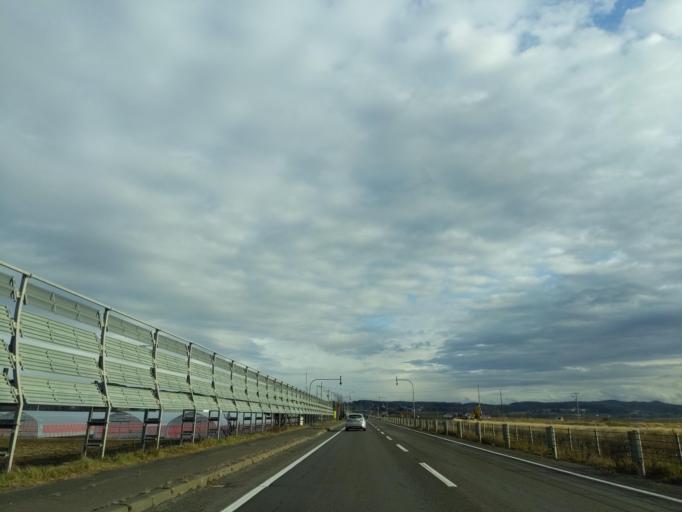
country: JP
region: Hokkaido
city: Kitahiroshima
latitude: 42.9566
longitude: 141.6996
